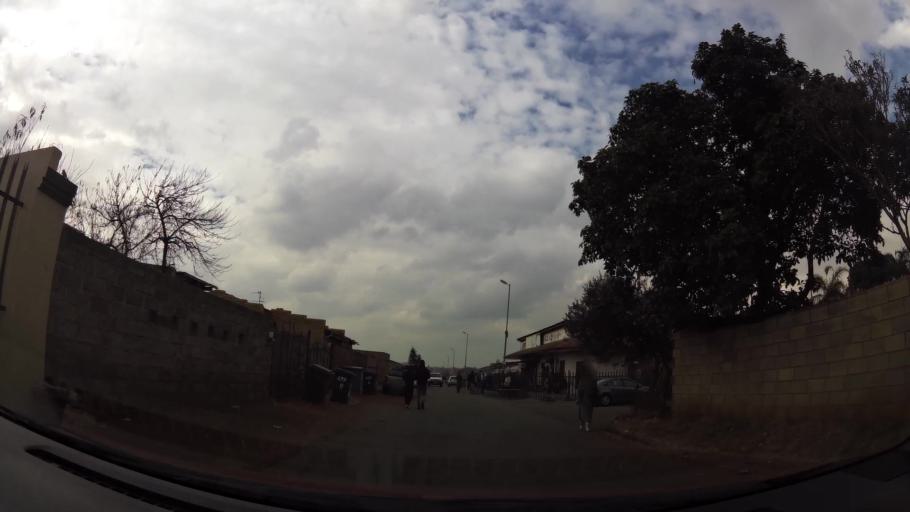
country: ZA
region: Gauteng
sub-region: City of Johannesburg Metropolitan Municipality
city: Soweto
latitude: -26.2492
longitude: 27.8320
